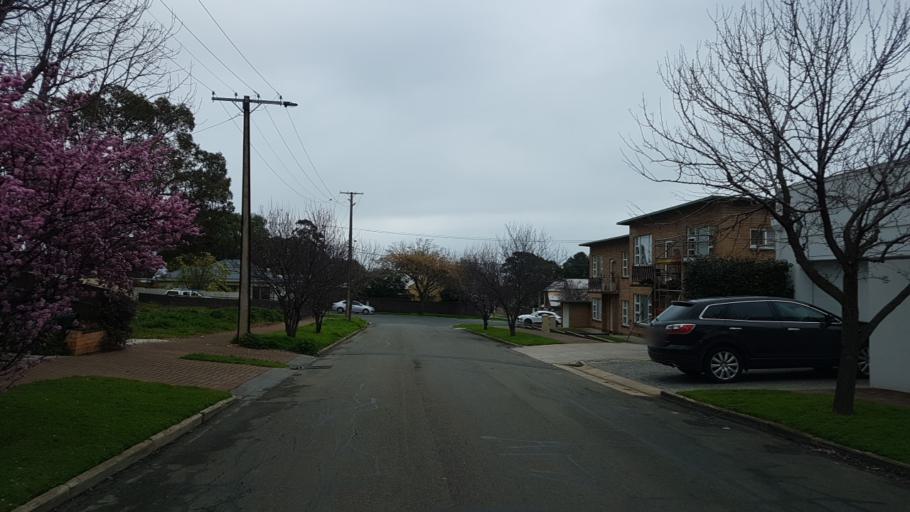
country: AU
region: South Australia
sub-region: Burnside
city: Linden Park
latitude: -34.9439
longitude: 138.6527
